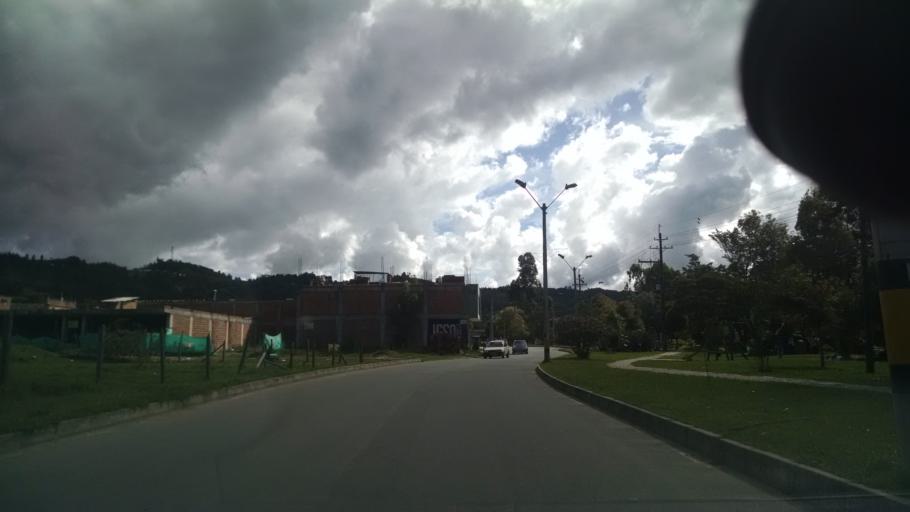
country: CO
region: Antioquia
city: El Retiro
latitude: 6.0635
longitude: -75.5025
